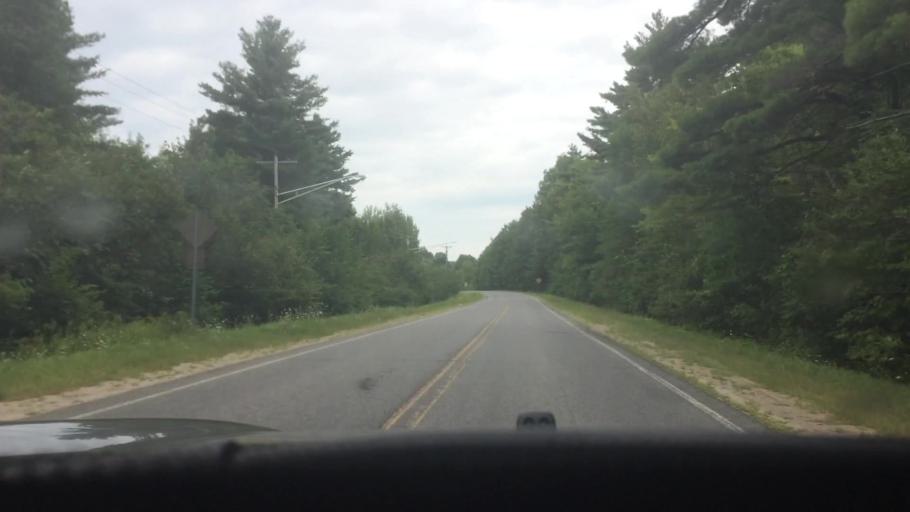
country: US
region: New York
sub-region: St. Lawrence County
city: Hannawa Falls
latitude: 44.5488
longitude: -74.9303
